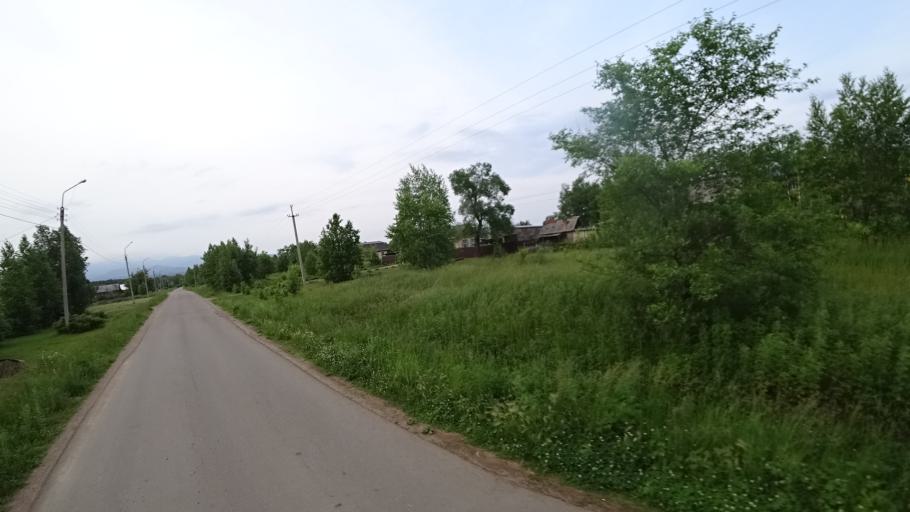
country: RU
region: Primorskiy
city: Novosysoyevka
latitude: 44.2341
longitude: 133.3595
